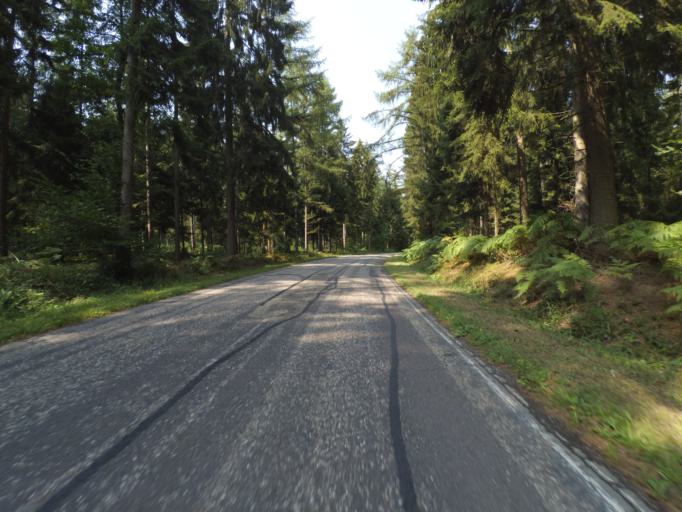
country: DE
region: Saarland
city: Saarhoelzbach
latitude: 49.5014
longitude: 6.6346
